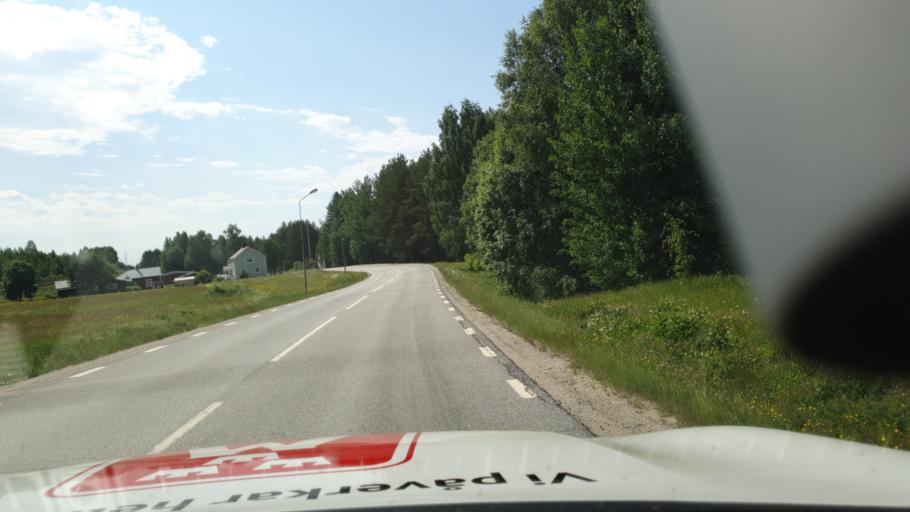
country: SE
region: Vaesterbotten
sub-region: Vindelns Kommun
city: Vindeln
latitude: 64.2268
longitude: 19.7080
